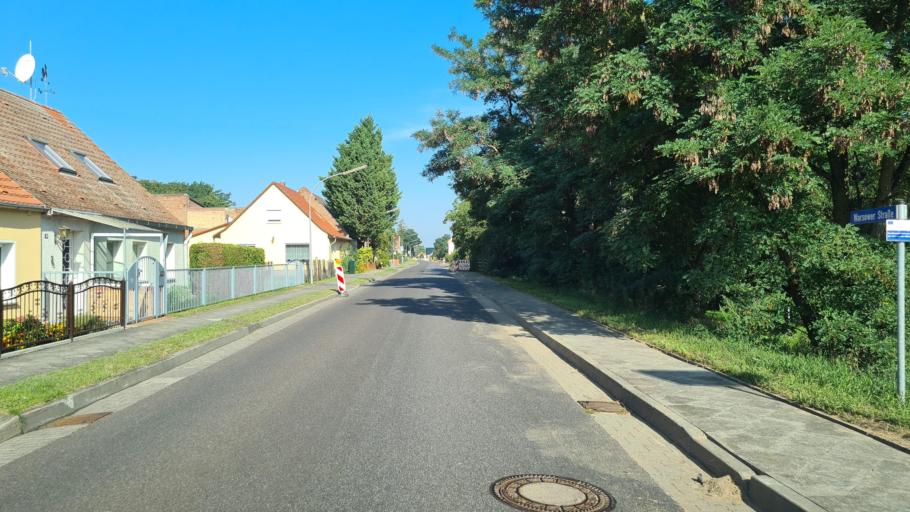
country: DE
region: Brandenburg
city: Friesack
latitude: 52.7240
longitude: 12.6315
